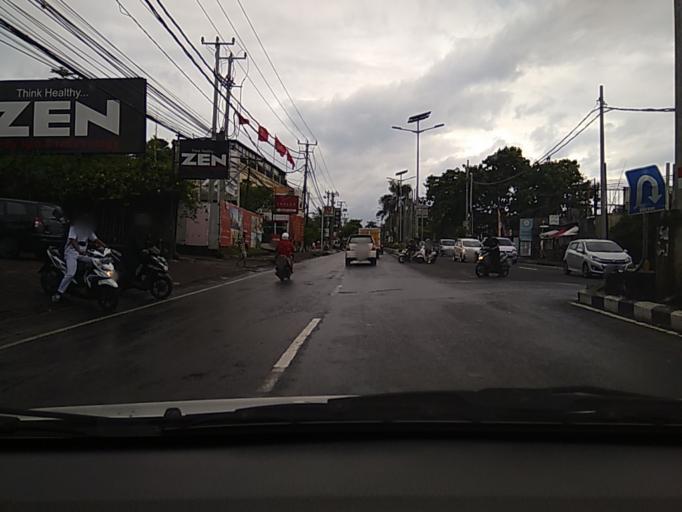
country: ID
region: Bali
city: Bualu
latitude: -8.7867
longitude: 115.2049
